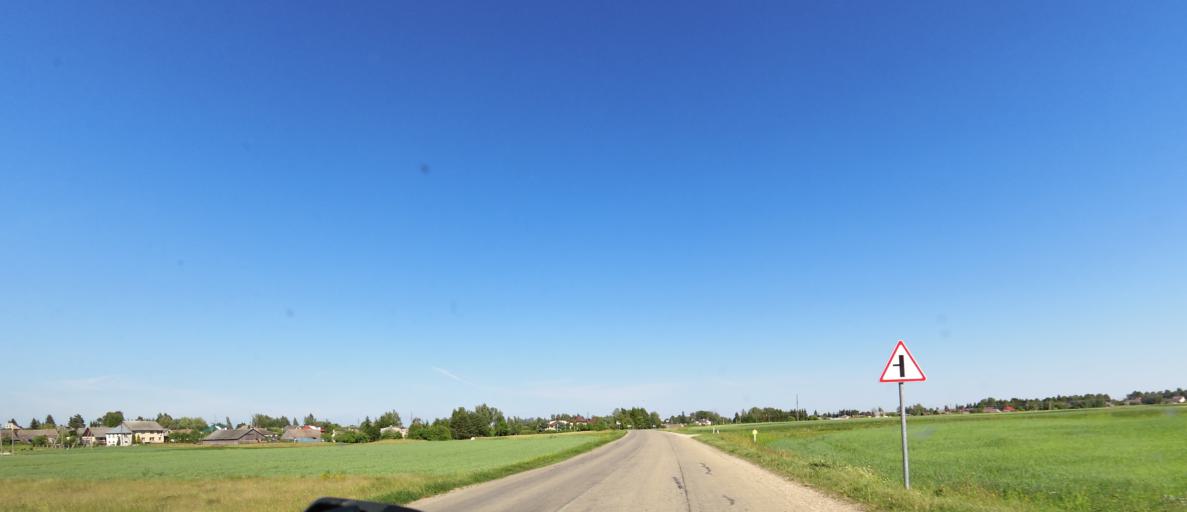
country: LT
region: Panevezys
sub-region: Birzai
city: Birzai
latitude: 56.2067
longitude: 24.7131
